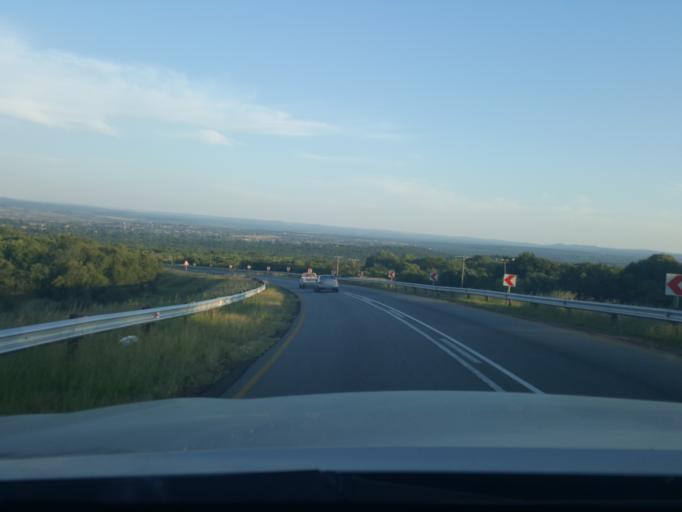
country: ZA
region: North-West
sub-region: Ngaka Modiri Molema District Municipality
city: Zeerust
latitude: -25.5129
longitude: 26.0617
